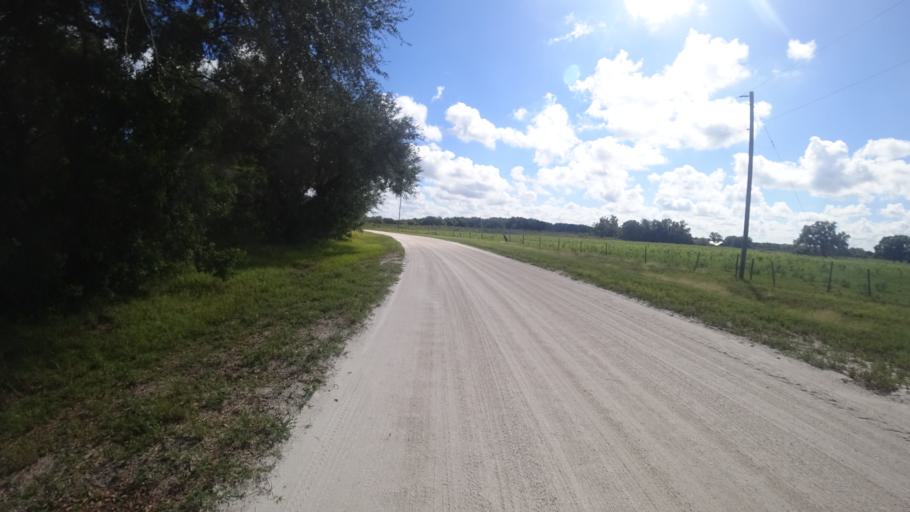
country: US
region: Florida
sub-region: DeSoto County
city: Arcadia
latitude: 27.3556
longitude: -82.1271
